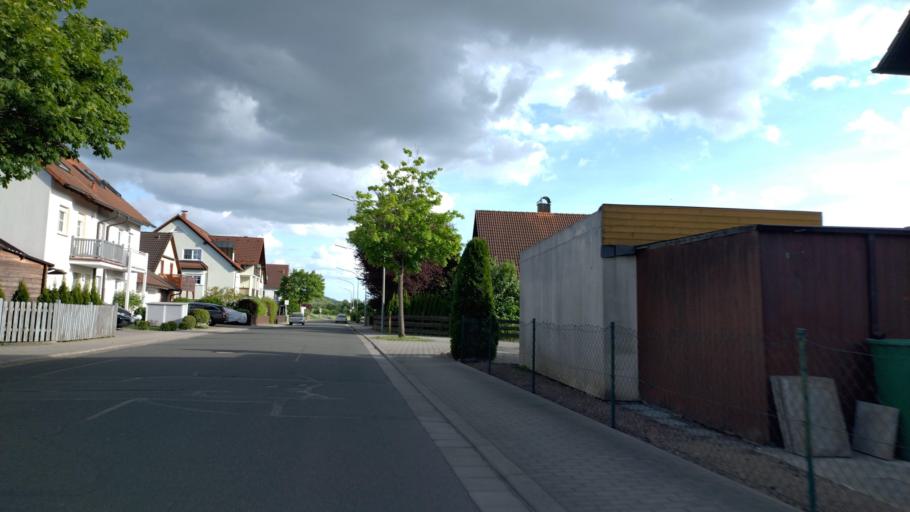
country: DE
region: Bavaria
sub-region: Upper Franconia
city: Bindlach
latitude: 49.9784
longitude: 11.6208
